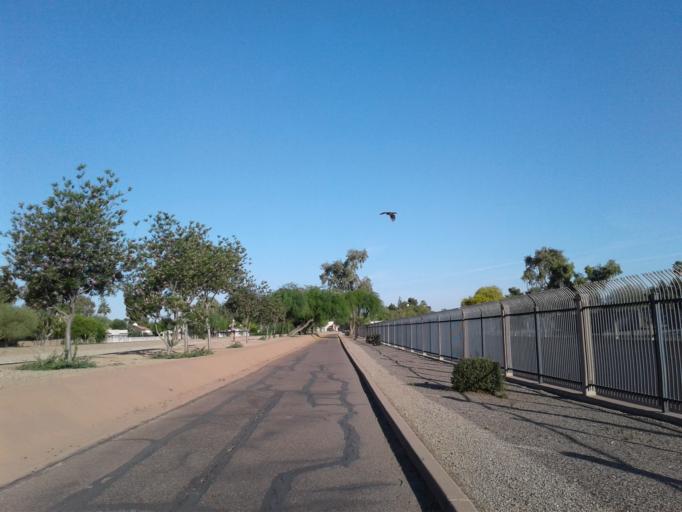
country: US
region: Arizona
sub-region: Maricopa County
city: Phoenix
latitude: 33.5596
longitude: -112.0703
